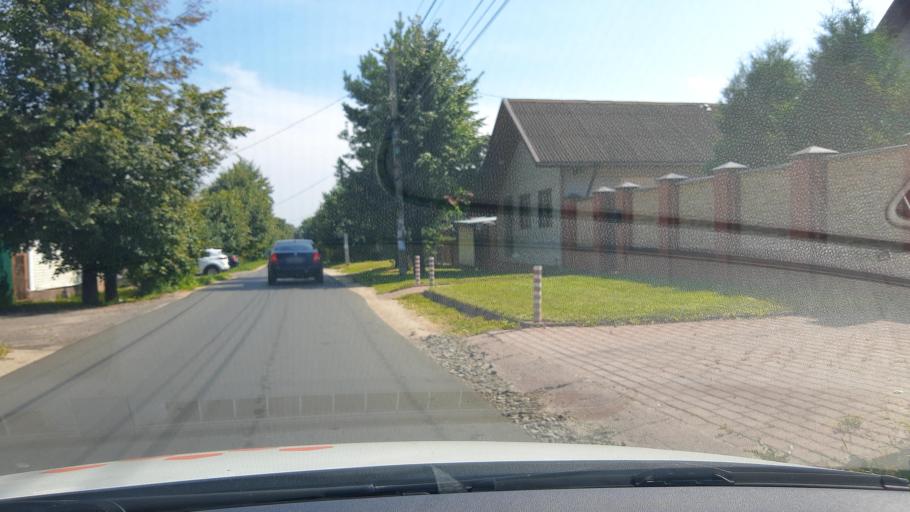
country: RU
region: Moskovskaya
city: Bronnitsy
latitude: 55.4251
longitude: 38.2580
